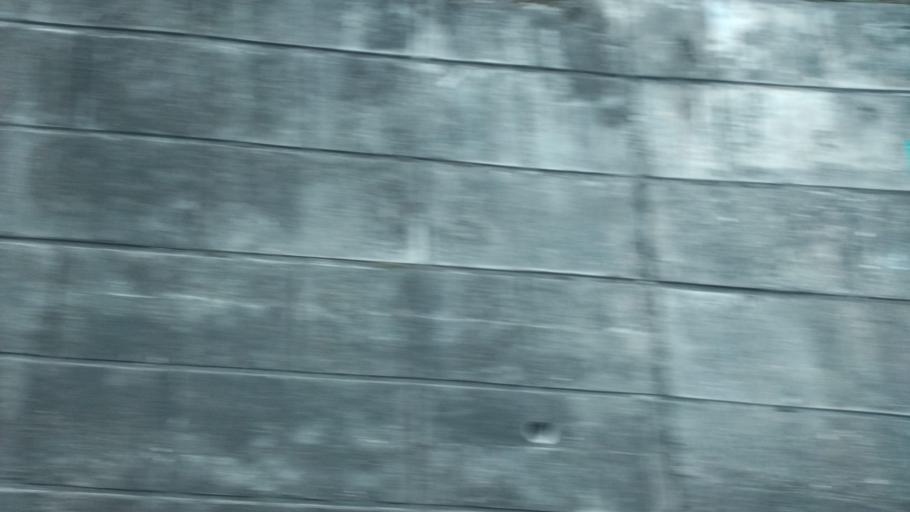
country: TW
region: Taiwan
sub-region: Hualien
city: Hualian
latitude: 24.2259
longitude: 121.7046
